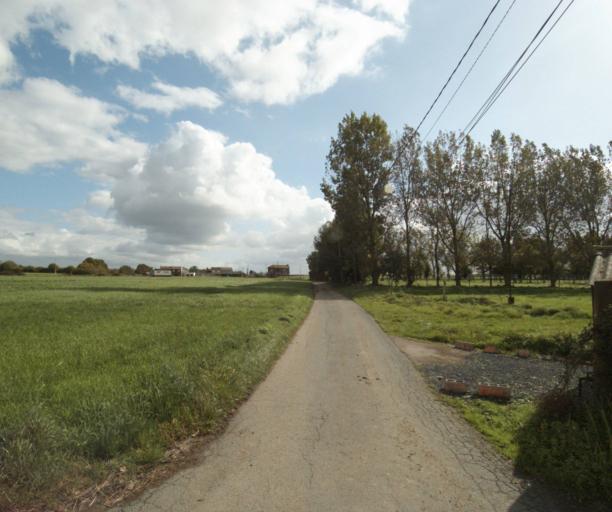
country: FR
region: Nord-Pas-de-Calais
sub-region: Departement du Nord
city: Frelinghien
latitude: 50.7251
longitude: 2.9373
